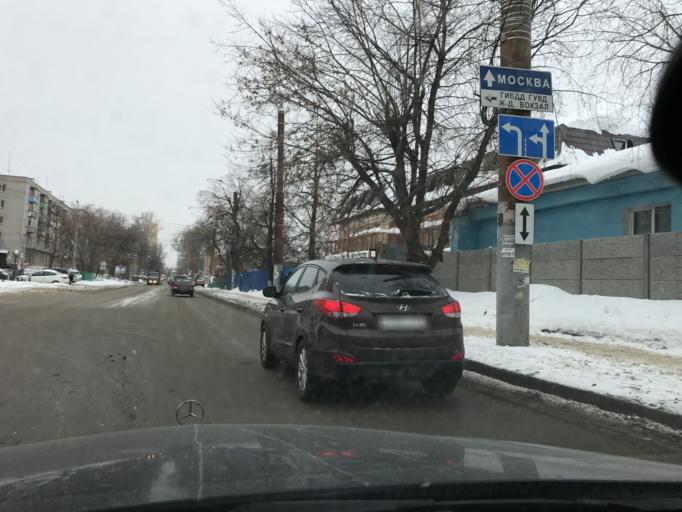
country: RU
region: Nizjnij Novgorod
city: Nizhniy Novgorod
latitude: 56.3327
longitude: 43.9622
